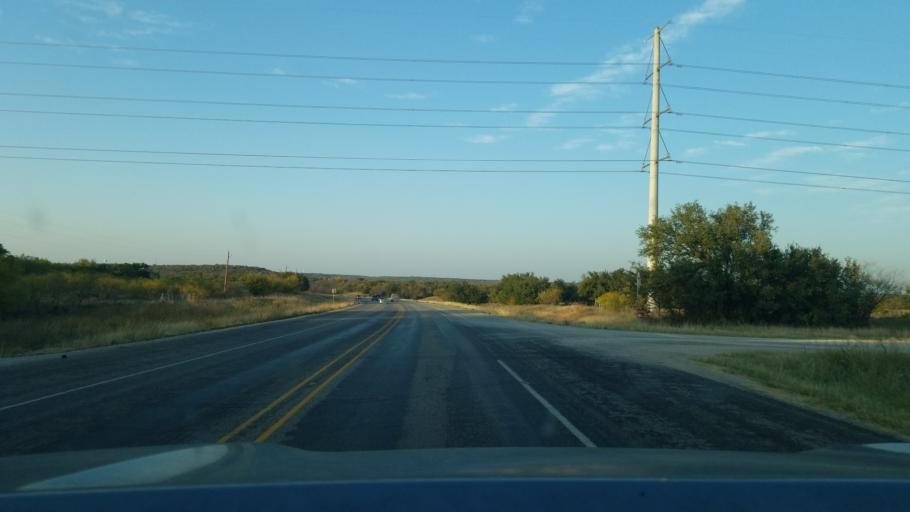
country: US
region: Texas
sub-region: Eastland County
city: Cisco
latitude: 32.3371
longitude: -98.9571
